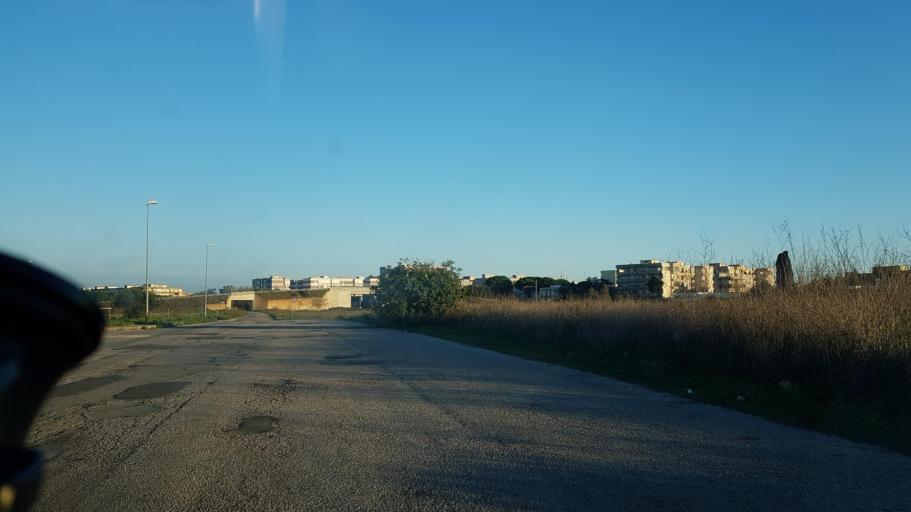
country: IT
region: Apulia
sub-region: Provincia di Brindisi
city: Mesagne
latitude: 40.5613
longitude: 17.7912
